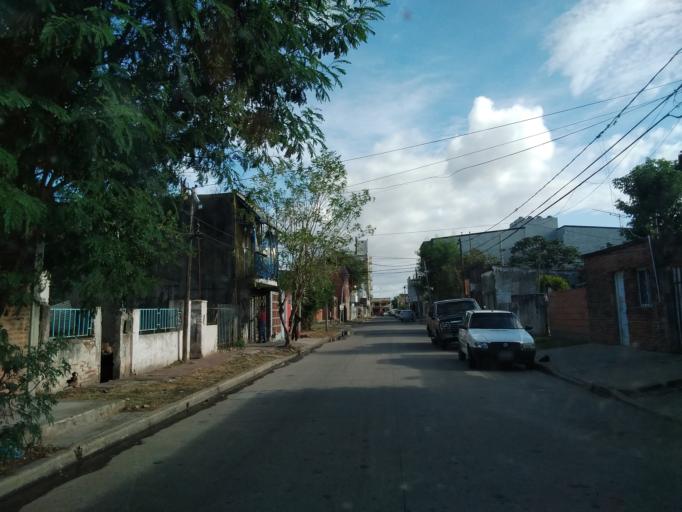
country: AR
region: Corrientes
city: Corrientes
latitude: -27.4657
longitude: -58.8127
